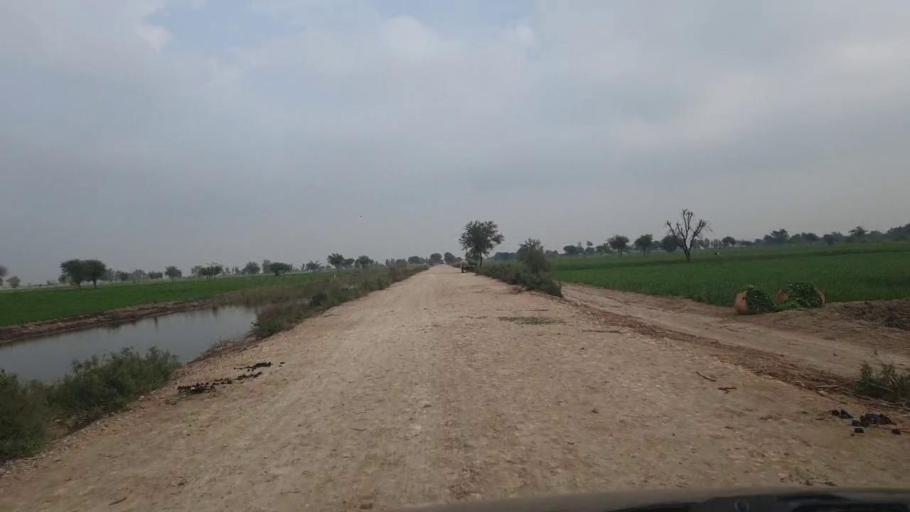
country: PK
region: Sindh
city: Shahdadpur
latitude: 25.8907
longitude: 68.6941
